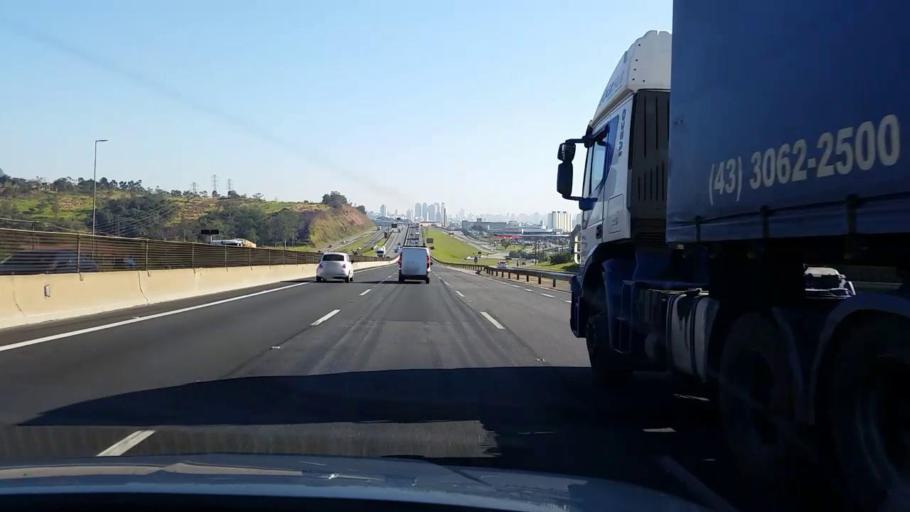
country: BR
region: Sao Paulo
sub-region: Jundiai
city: Jundiai
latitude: -23.2322
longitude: -46.8721
